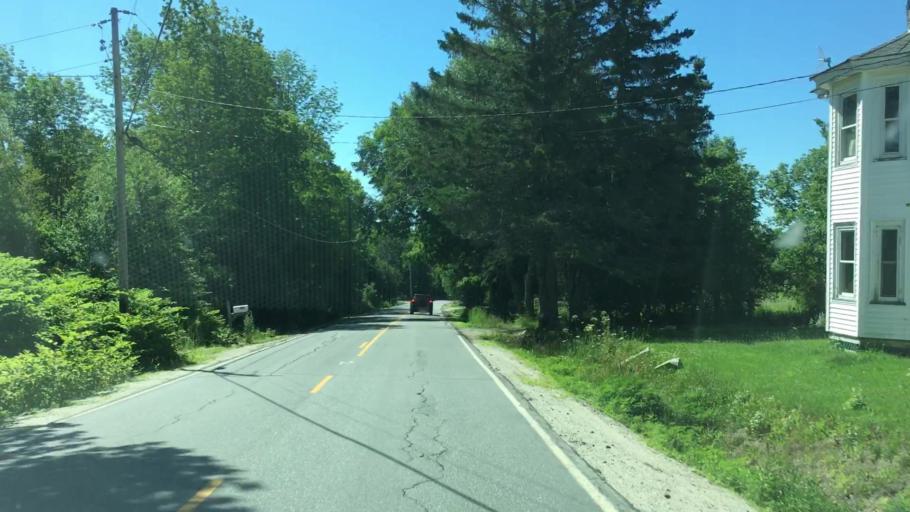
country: US
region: Maine
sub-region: Hancock County
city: Penobscot
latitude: 44.4365
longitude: -68.6325
